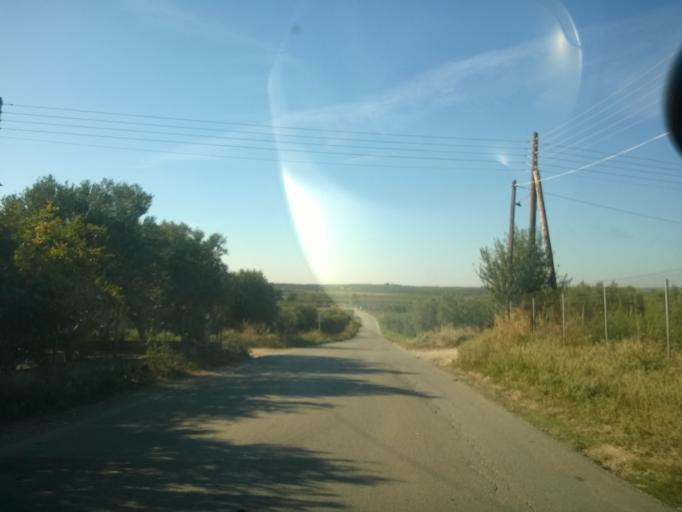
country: GR
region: Central Macedonia
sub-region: Nomos Chalkidikis
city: Nea Kallikrateia
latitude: 40.3382
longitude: 23.0497
